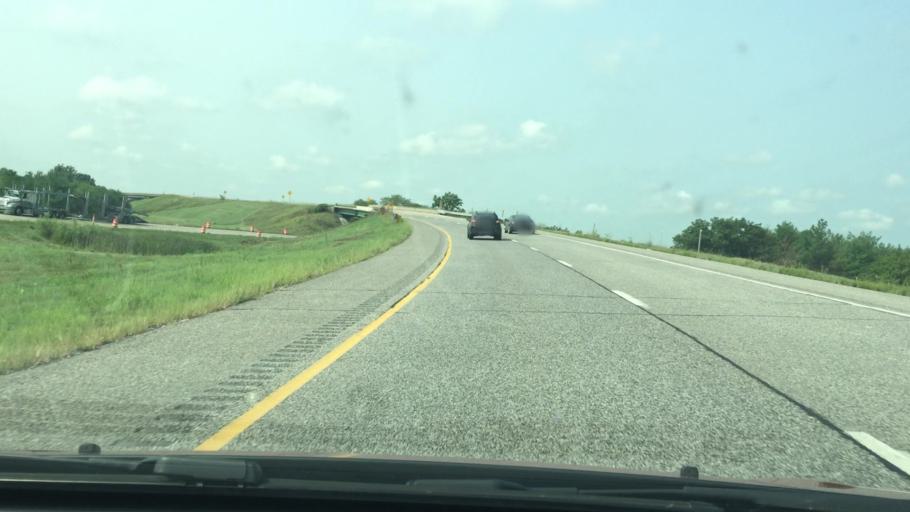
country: US
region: Iowa
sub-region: Scott County
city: Walcott
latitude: 41.6036
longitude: -90.6725
